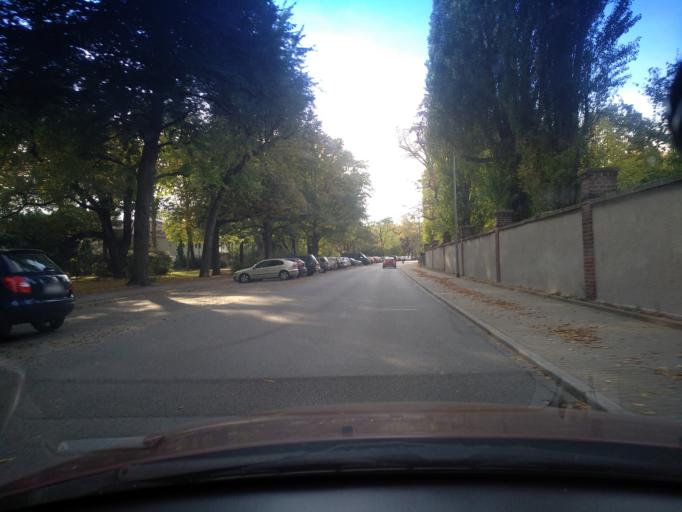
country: DE
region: Saxony
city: Bautzen
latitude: 51.1835
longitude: 14.4334
